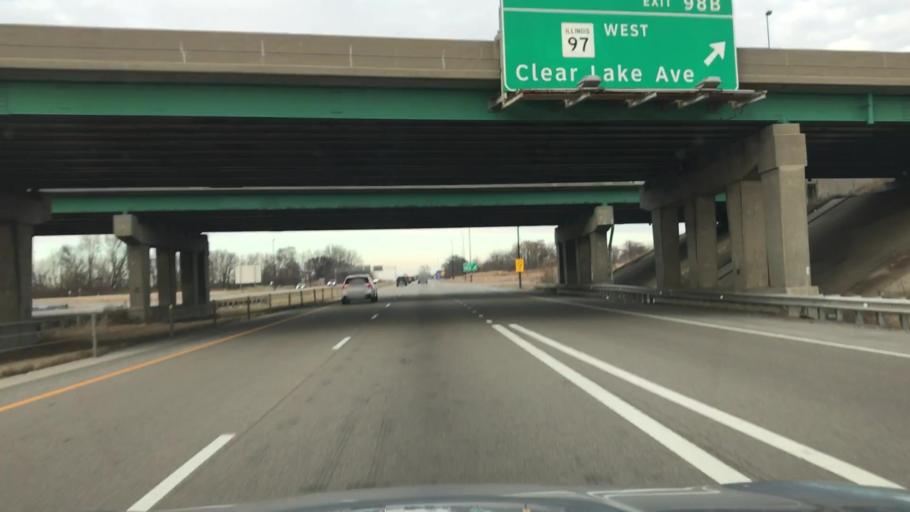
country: US
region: Illinois
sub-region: Sangamon County
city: Grandview
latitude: 39.8017
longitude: -89.5951
